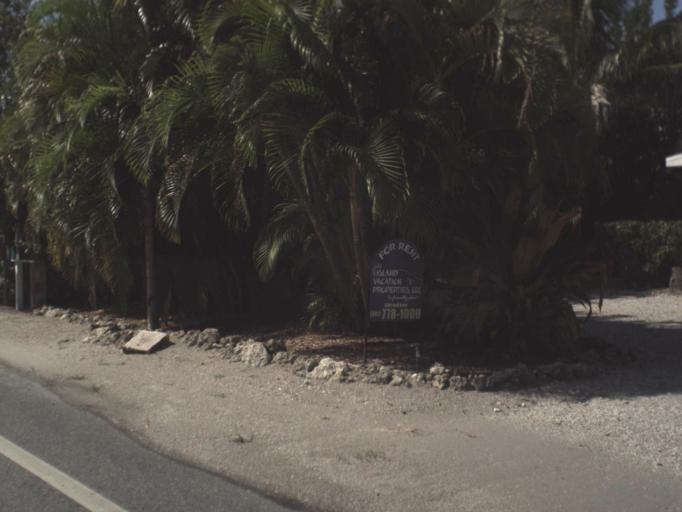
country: US
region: Florida
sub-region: Manatee County
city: Holmes Beach
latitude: 27.4874
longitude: -82.7063
